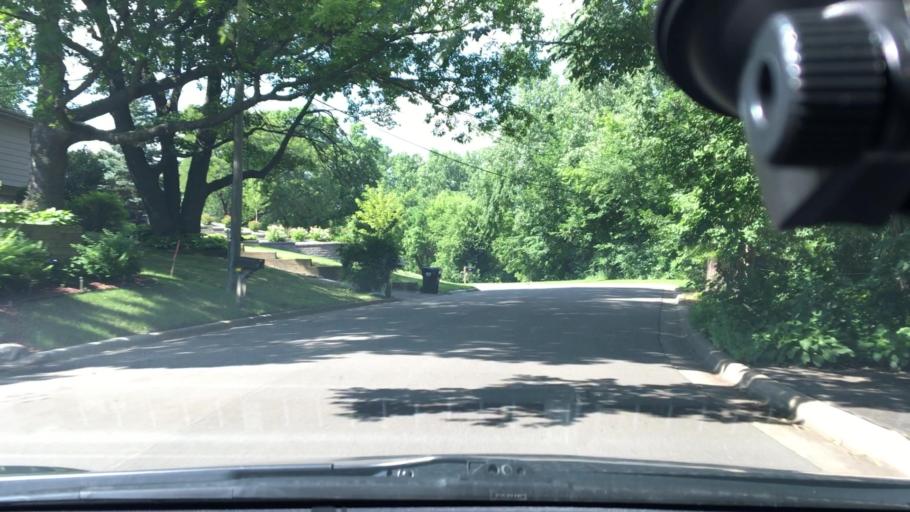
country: US
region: Minnesota
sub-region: Hennepin County
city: Golden Valley
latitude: 44.9951
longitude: -93.3871
